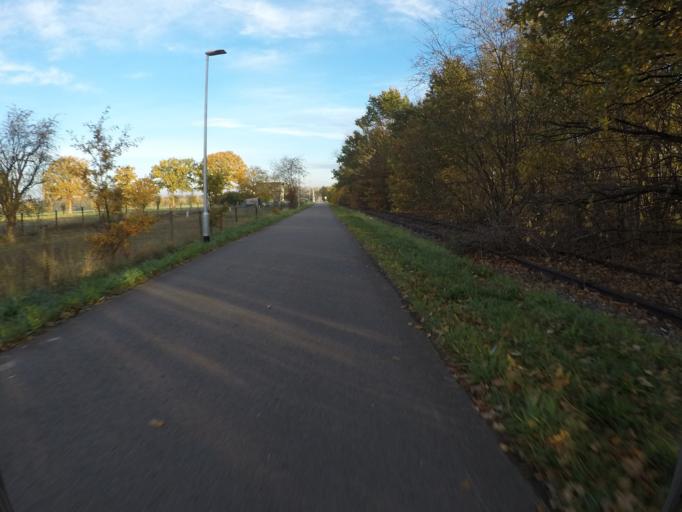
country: BE
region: Flanders
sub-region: Provincie Antwerpen
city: Olen
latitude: 51.1278
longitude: 4.8249
